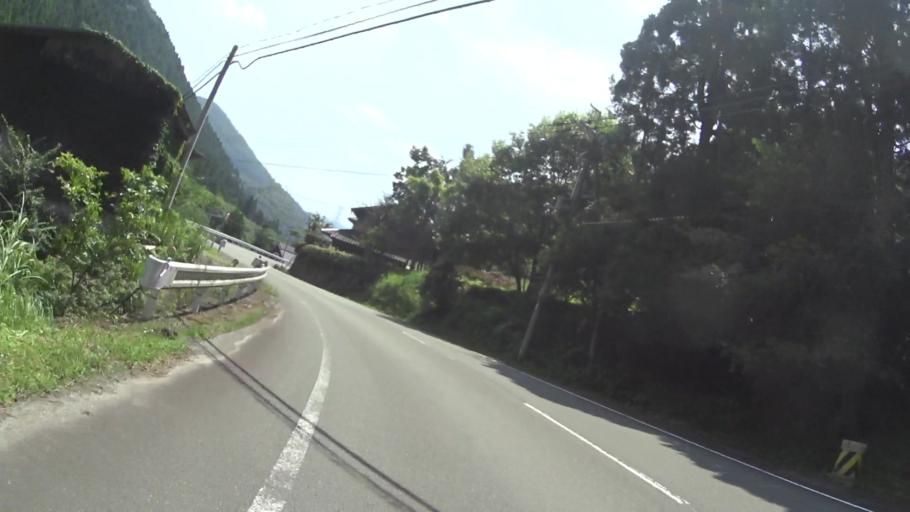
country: JP
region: Kyoto
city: Ayabe
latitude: 35.2885
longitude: 135.4265
